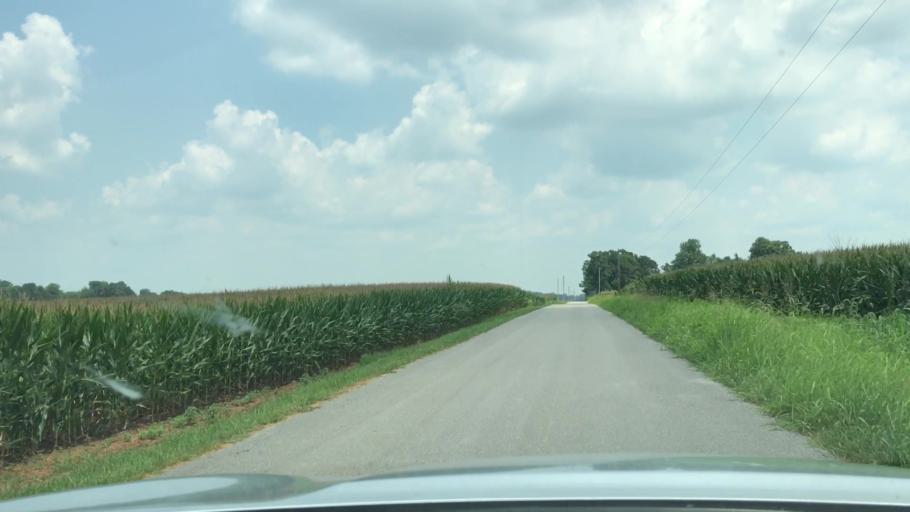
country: US
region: Kentucky
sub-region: Todd County
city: Elkton
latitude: 36.7621
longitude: -87.1202
